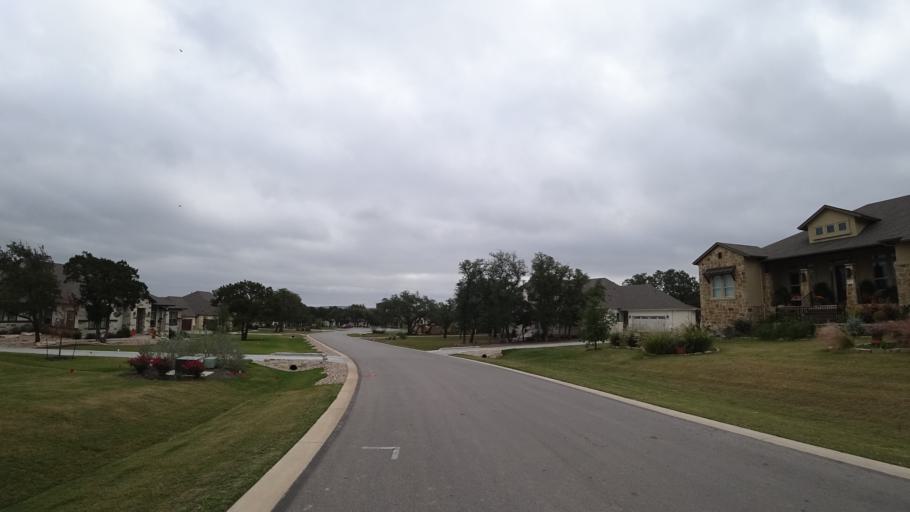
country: US
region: Texas
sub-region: Travis County
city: Barton Creek
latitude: 30.2559
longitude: -97.9130
